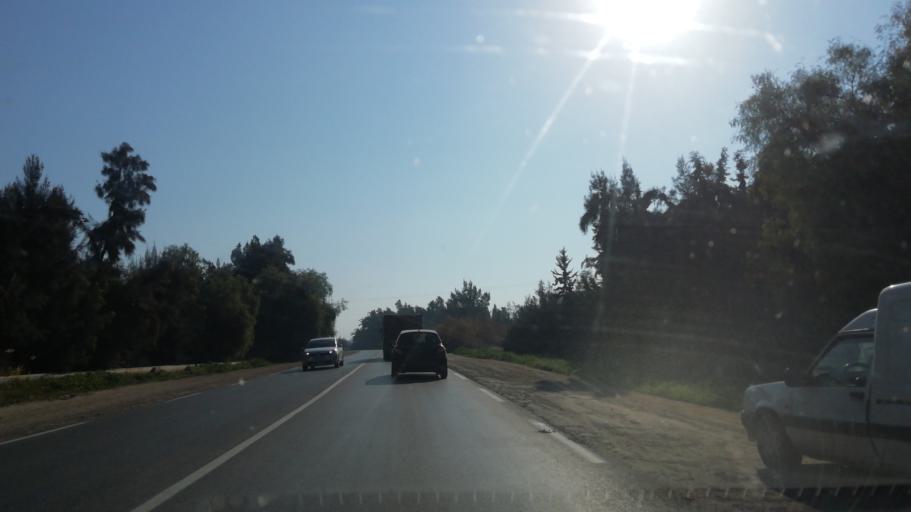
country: DZ
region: Relizane
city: Relizane
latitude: 35.7258
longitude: 0.4799
